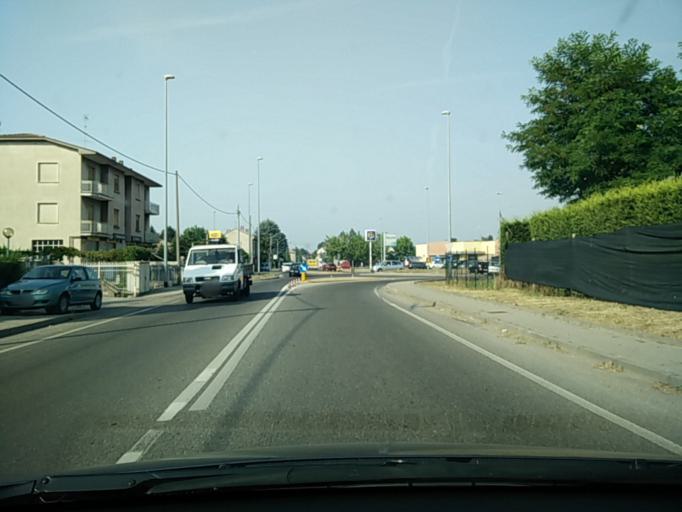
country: IT
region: Lombardy
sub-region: Provincia di Pavia
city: Casteggio
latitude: 45.0110
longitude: 9.1151
